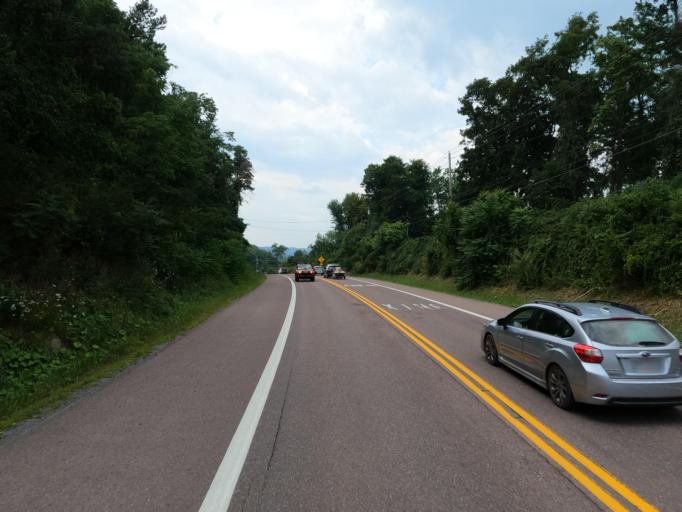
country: US
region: Maryland
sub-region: Garrett County
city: Mountain Lake Park
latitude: 39.5217
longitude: -79.3317
